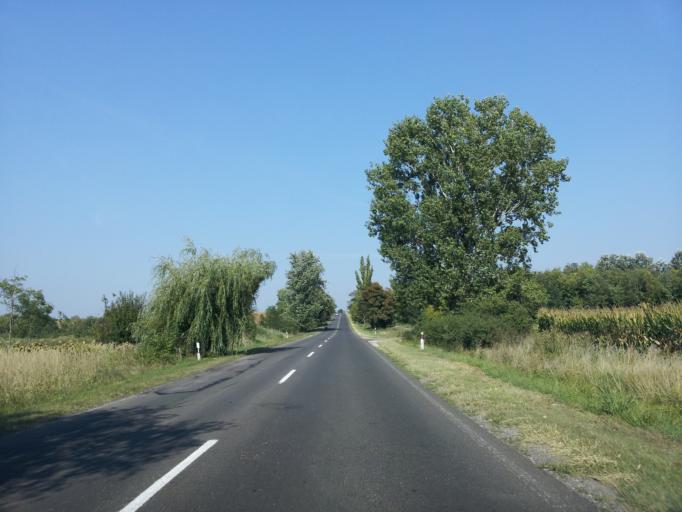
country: HU
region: Fejer
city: Lepseny
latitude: 47.0124
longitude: 18.2705
